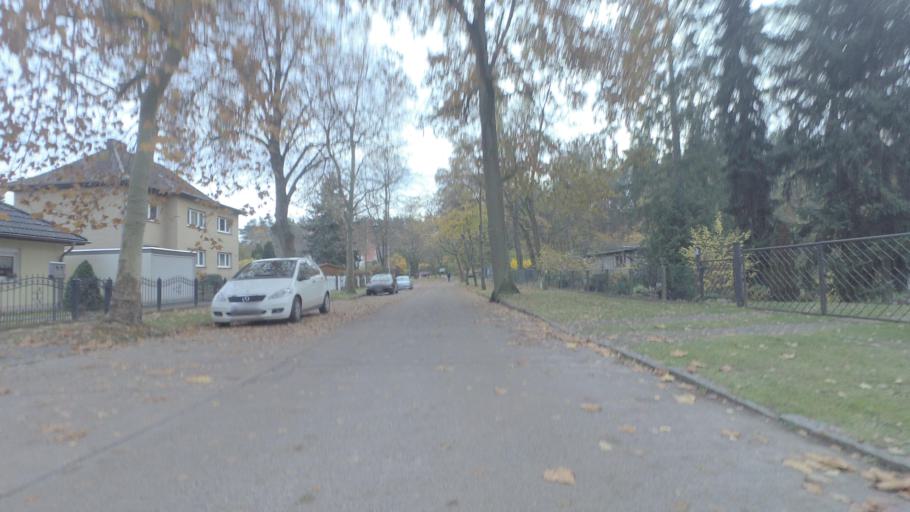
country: DE
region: Brandenburg
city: Rangsdorf
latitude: 52.3231
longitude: 13.4160
